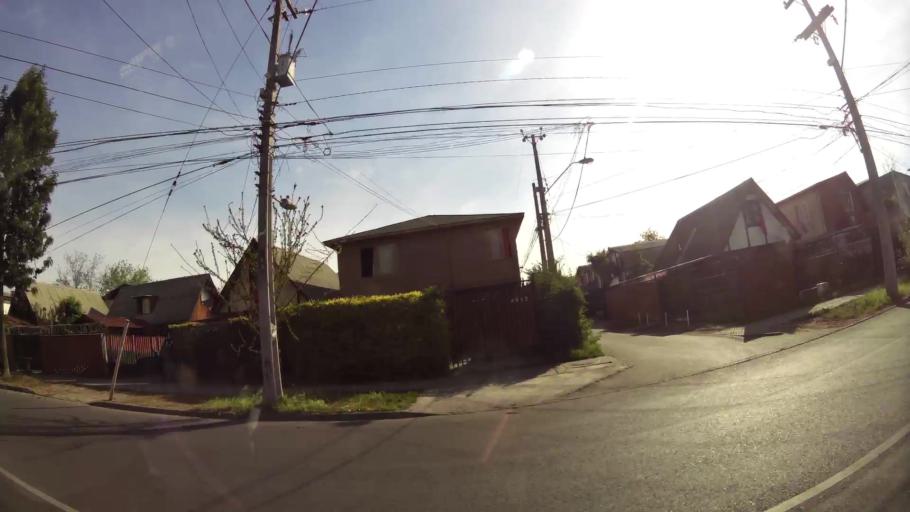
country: CL
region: Santiago Metropolitan
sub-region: Provincia de Santiago
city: Villa Presidente Frei, Nunoa, Santiago, Chile
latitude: -33.5311
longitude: -70.5790
